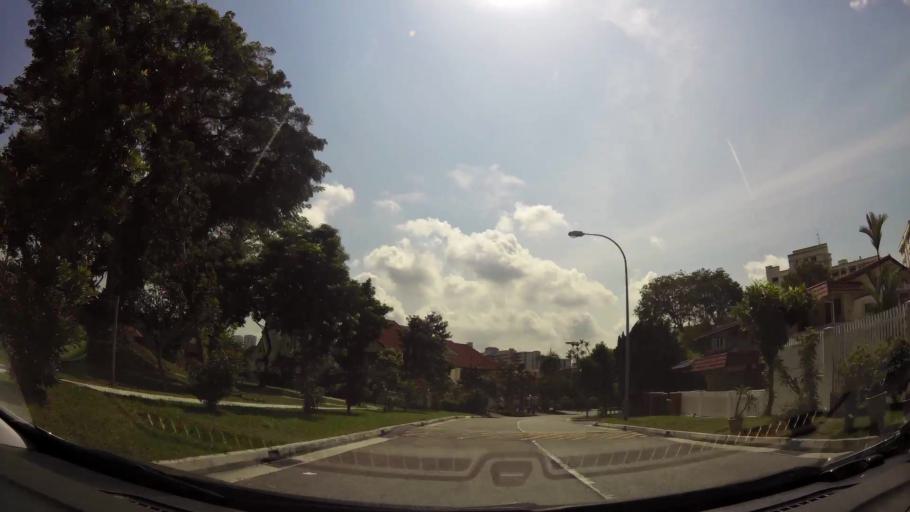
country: SG
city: Singapore
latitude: 1.3726
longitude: 103.8391
